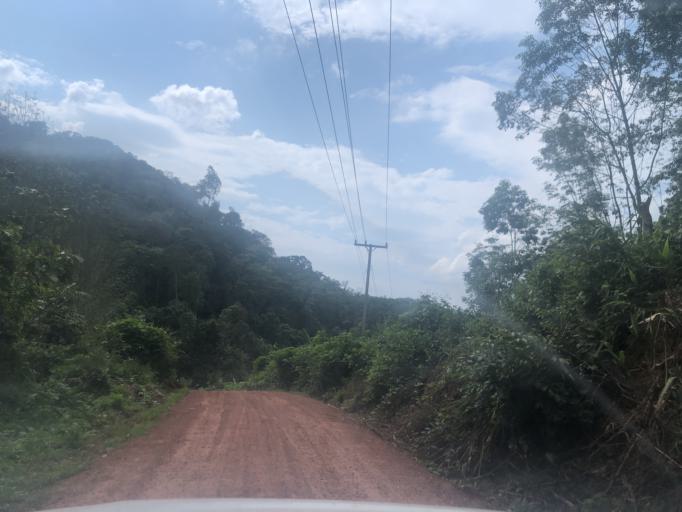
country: LA
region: Oudomxai
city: Muang La
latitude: 21.2444
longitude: 101.9350
